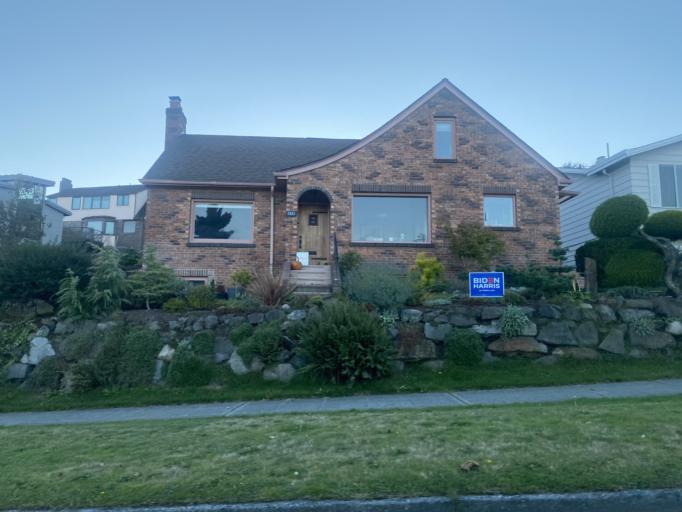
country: US
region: Washington
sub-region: King County
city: Seattle
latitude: 47.6417
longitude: -122.4040
